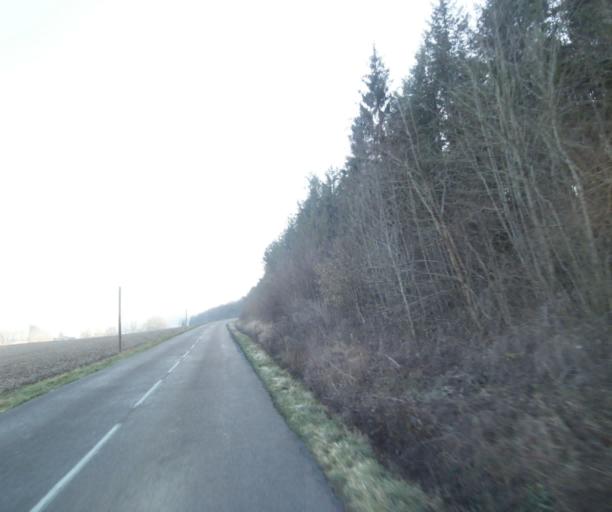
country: FR
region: Champagne-Ardenne
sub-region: Departement de la Haute-Marne
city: Bienville
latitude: 48.5630
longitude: 5.0817
